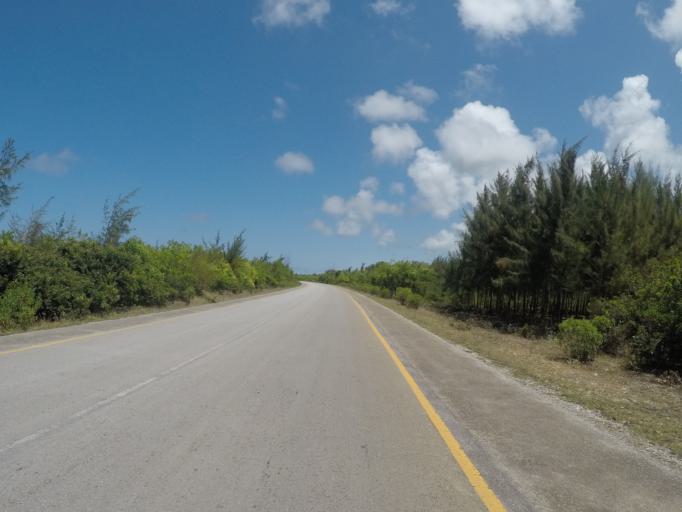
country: TZ
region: Zanzibar Central/South
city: Nganane
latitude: -6.3875
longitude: 39.5596
